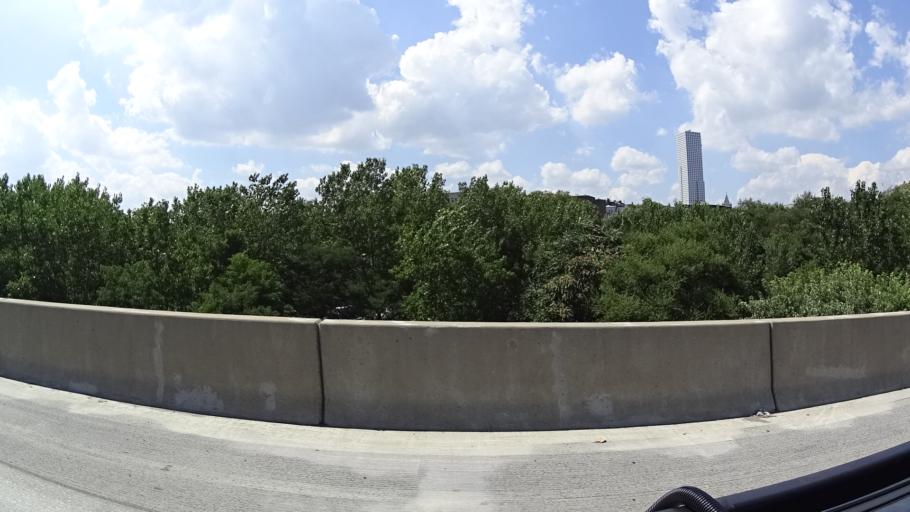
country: US
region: New Jersey
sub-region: Hudson County
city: Jersey City
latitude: 40.7276
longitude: -74.0529
